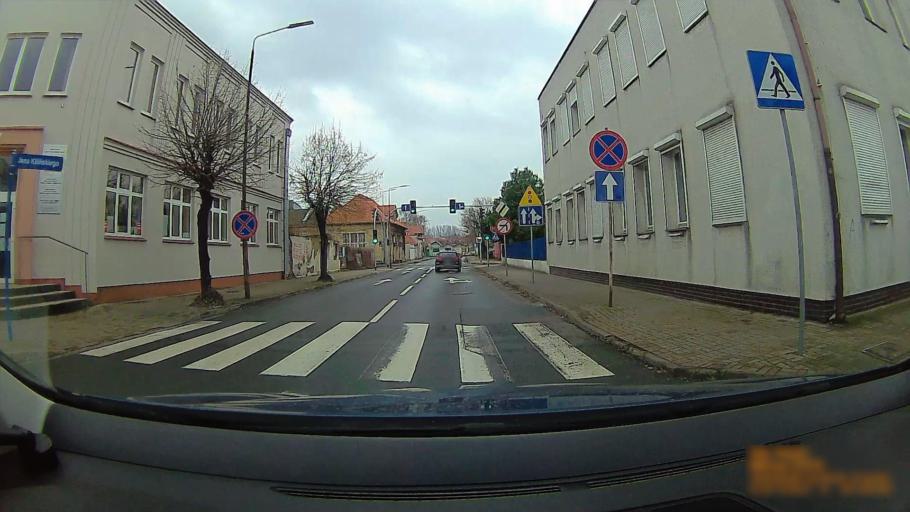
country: PL
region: Greater Poland Voivodeship
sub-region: Konin
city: Konin
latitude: 52.2102
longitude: 18.2514
